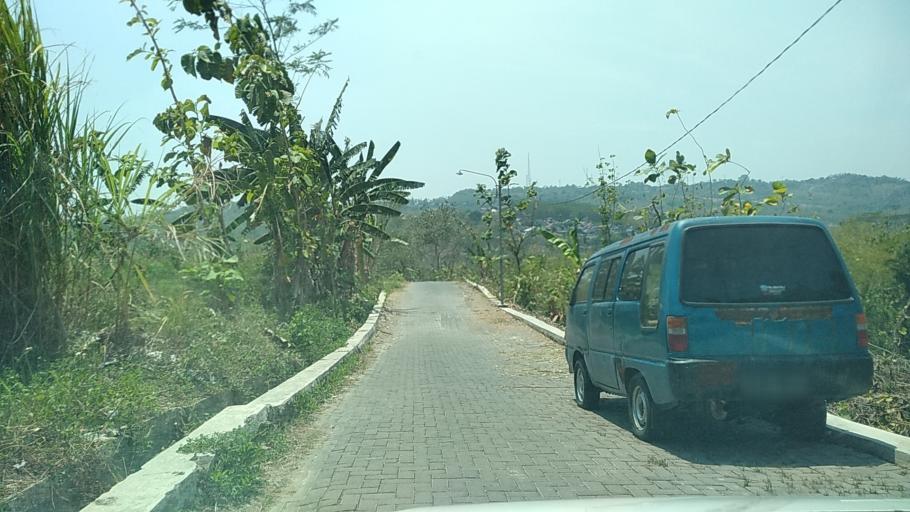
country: ID
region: Central Java
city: Semarang
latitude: -7.0297
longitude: 110.3745
